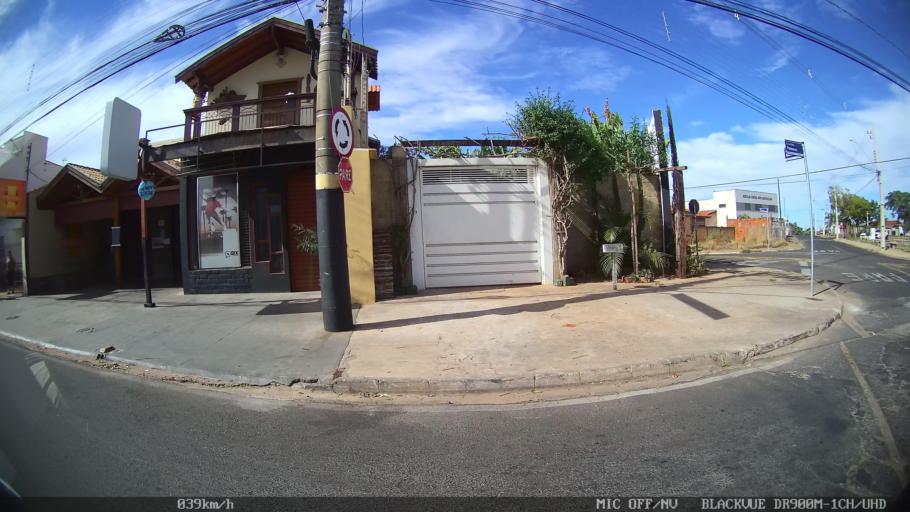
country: BR
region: Sao Paulo
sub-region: Catanduva
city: Catanduva
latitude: -21.1239
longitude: -48.9467
